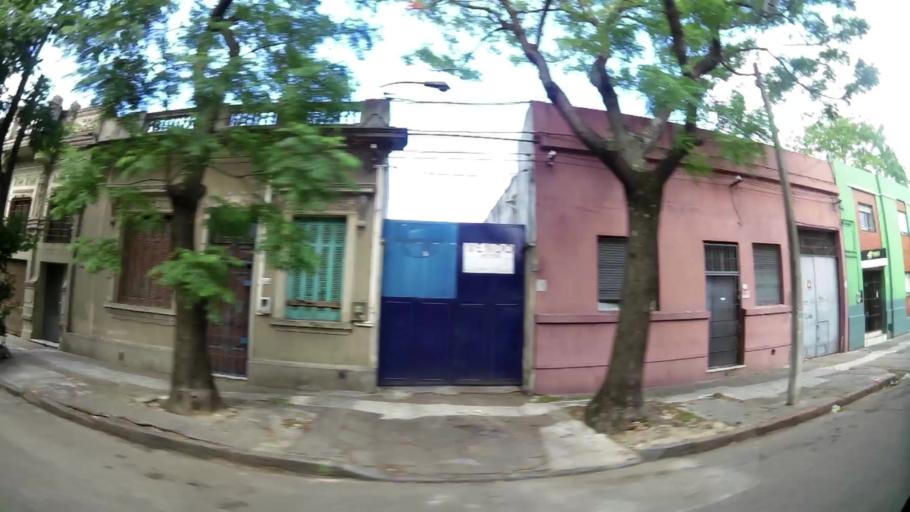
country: UY
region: Montevideo
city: Montevideo
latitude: -34.8884
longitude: -56.1804
